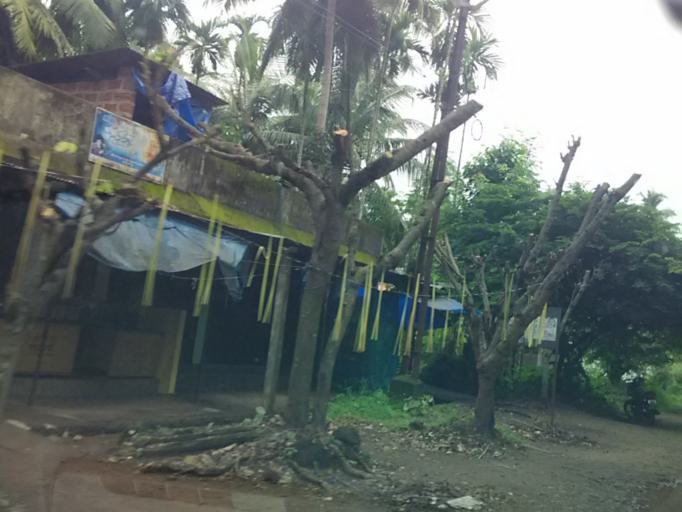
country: IN
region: Kerala
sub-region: Kozhikode
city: Kunnamangalam
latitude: 11.3134
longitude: 75.9234
